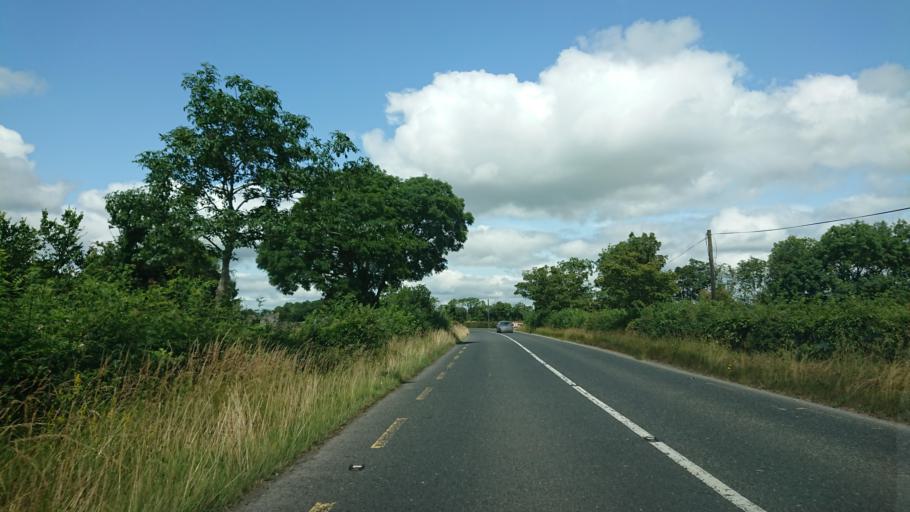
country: IE
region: Leinster
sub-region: Kildare
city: Kilcock
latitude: 53.3678
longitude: -6.6995
